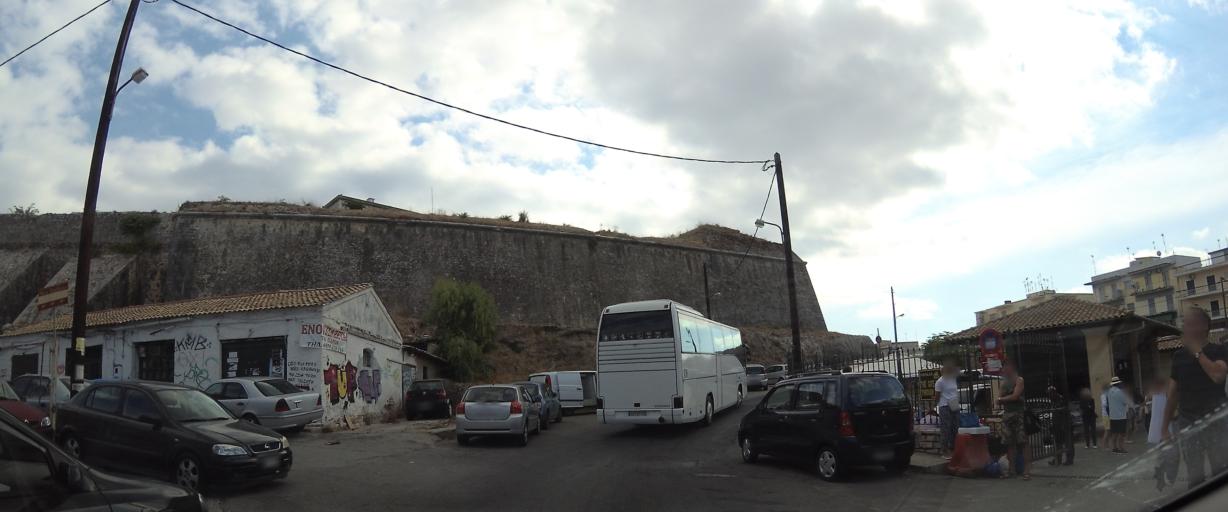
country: GR
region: Ionian Islands
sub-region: Nomos Kerkyras
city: Kerkyra
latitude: 39.6238
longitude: 19.9175
